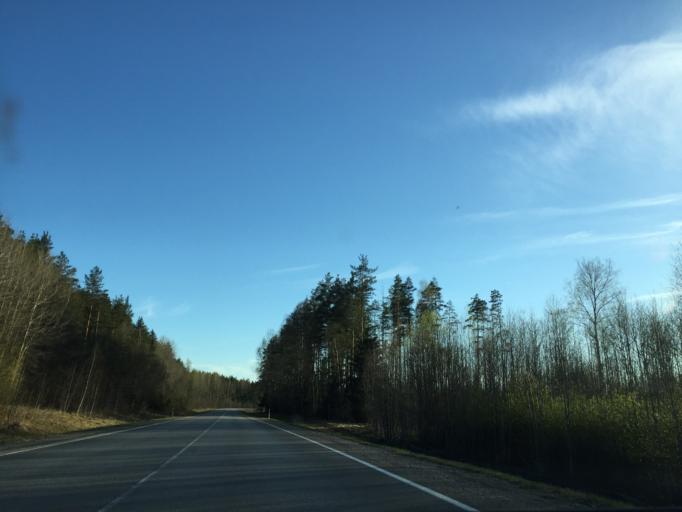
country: LV
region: Strenci
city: Strenci
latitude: 57.6001
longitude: 25.5745
